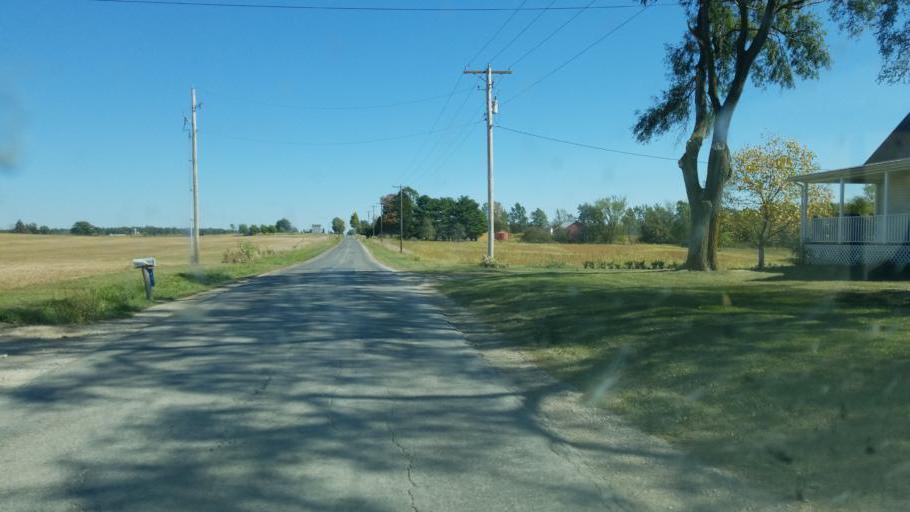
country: US
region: Ohio
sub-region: Huron County
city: Greenwich
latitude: 40.9930
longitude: -82.4991
